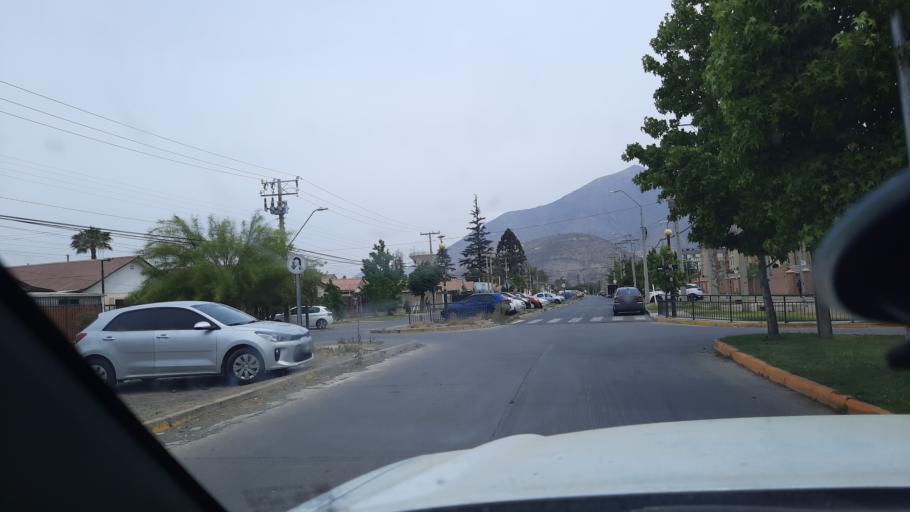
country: CL
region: Valparaiso
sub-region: Provincia de San Felipe
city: San Felipe
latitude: -32.7573
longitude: -70.7220
